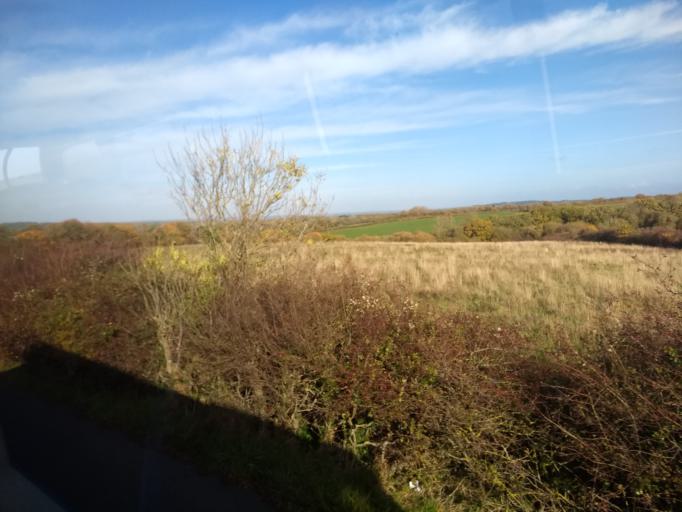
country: GB
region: England
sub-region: Isle of Wight
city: Shalfleet
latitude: 50.6828
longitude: -1.4146
